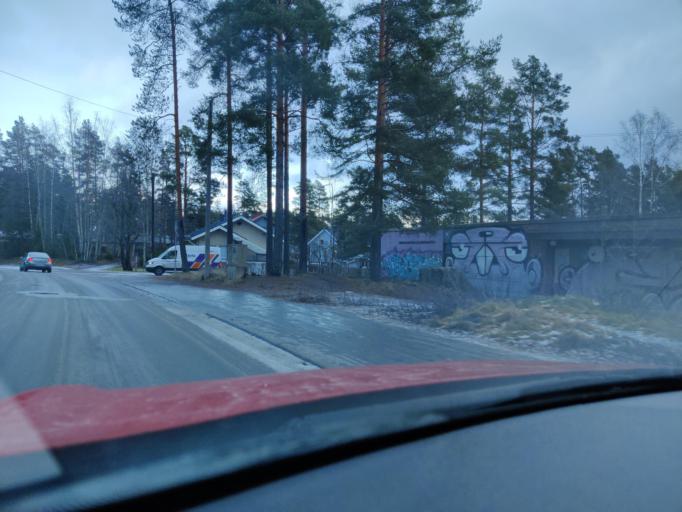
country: FI
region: Pirkanmaa
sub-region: Tampere
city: Nokia
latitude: 61.4664
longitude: 23.4993
